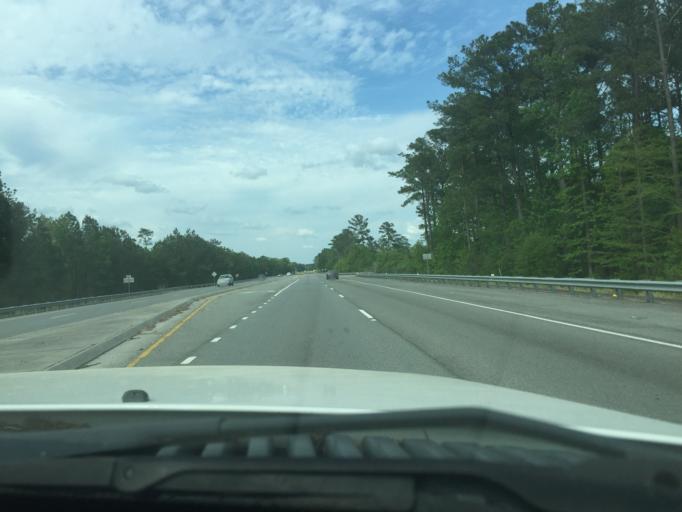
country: US
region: Georgia
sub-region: Bryan County
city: Richmond Hill
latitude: 31.9843
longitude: -81.2831
